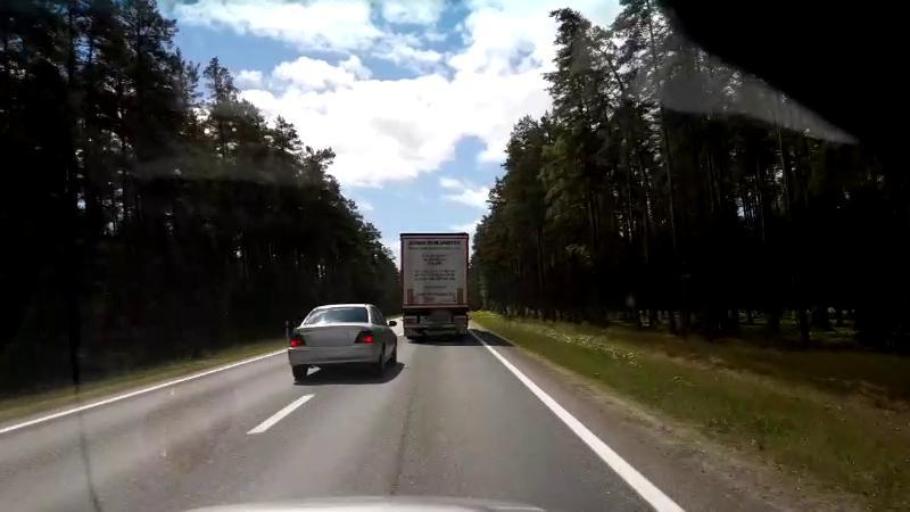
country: LV
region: Salacgrivas
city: Salacgriva
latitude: 57.5590
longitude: 24.4337
